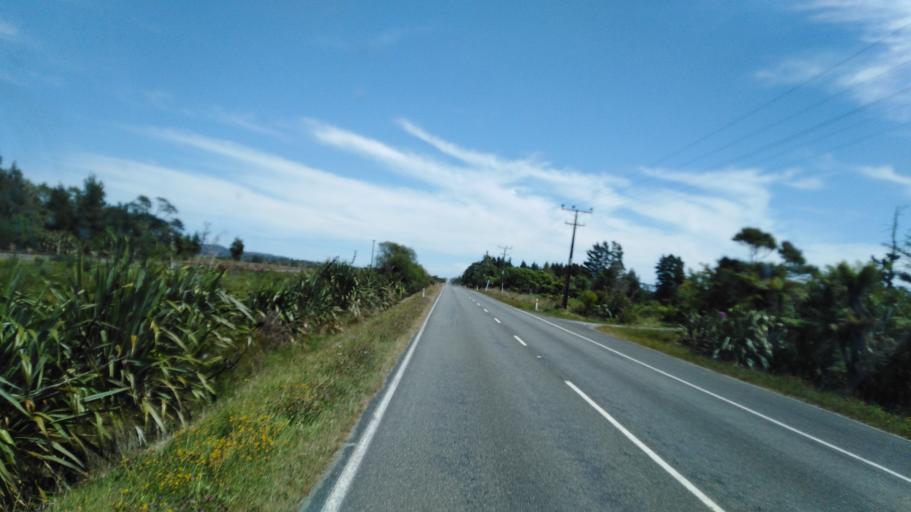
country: NZ
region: West Coast
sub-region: Buller District
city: Westport
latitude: -41.7391
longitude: 171.7008
